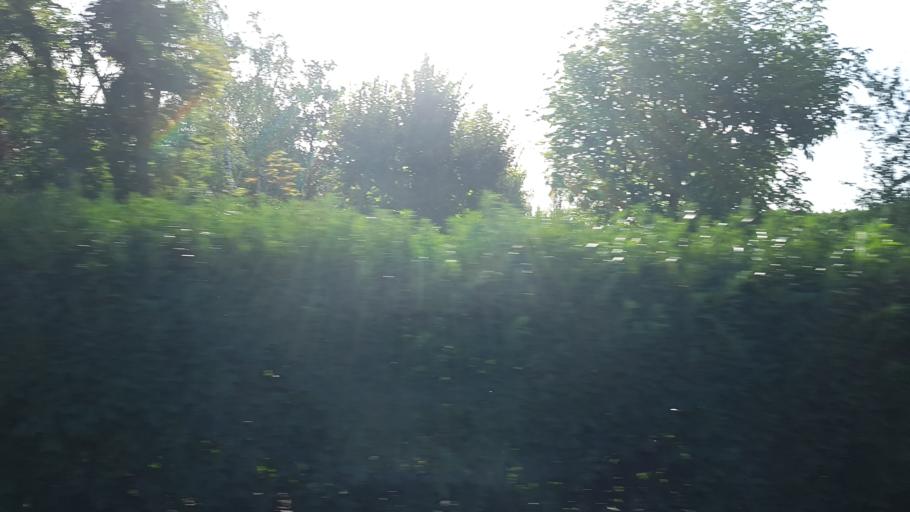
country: IT
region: Emilia-Romagna
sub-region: Provincia di Modena
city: Cavezzo
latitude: 44.8134
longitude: 11.0331
